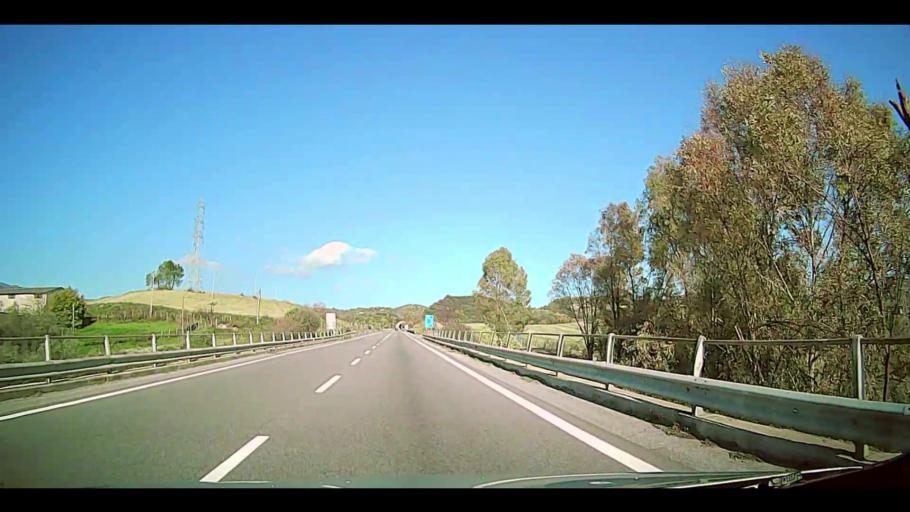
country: IT
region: Calabria
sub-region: Provincia di Crotone
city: Cotronei
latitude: 39.1899
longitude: 16.8159
